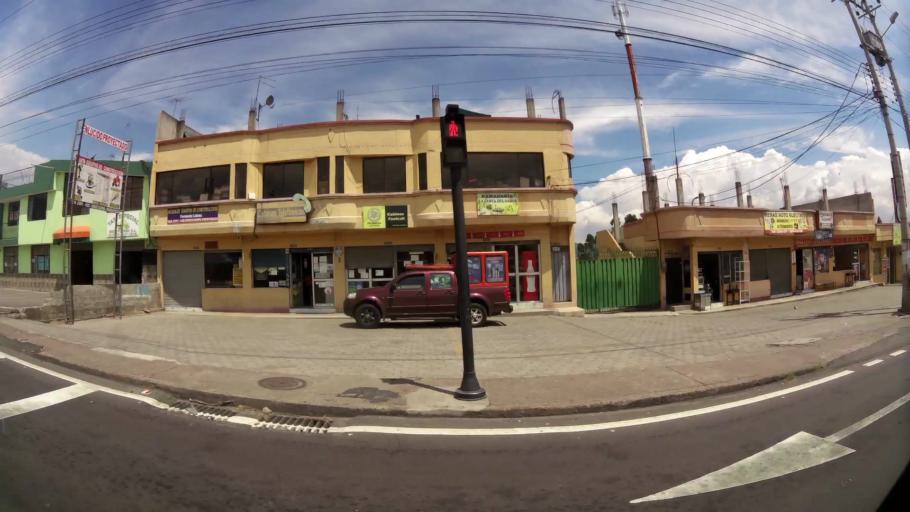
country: EC
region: Pichincha
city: Sangolqui
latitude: -0.2025
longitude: -78.3687
